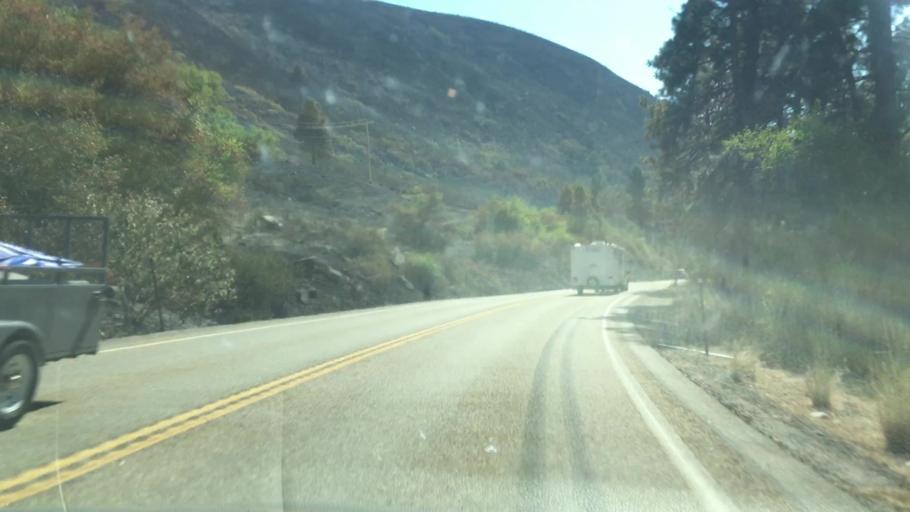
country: US
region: Idaho
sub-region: Gem County
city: Emmett
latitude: 44.0103
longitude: -116.1625
